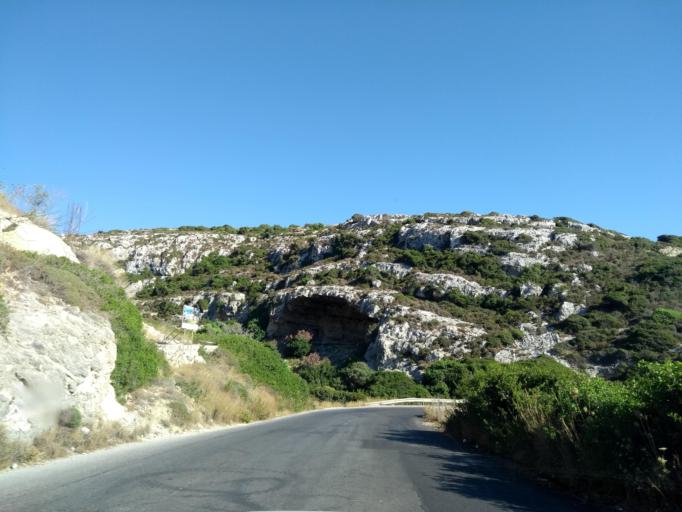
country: GR
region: Crete
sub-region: Nomos Chanias
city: Pithari
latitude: 35.5562
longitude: 24.0886
